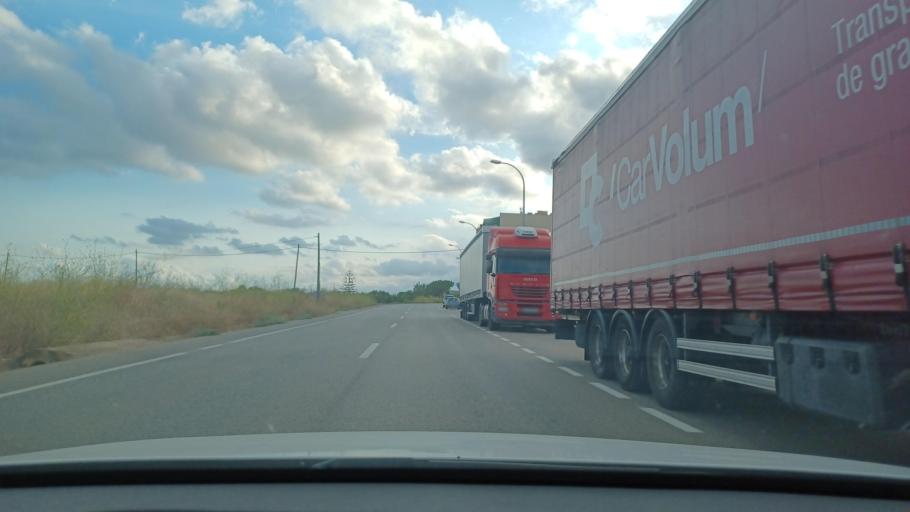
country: ES
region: Catalonia
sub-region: Provincia de Tarragona
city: Alcanar
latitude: 40.5405
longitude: 0.4846
